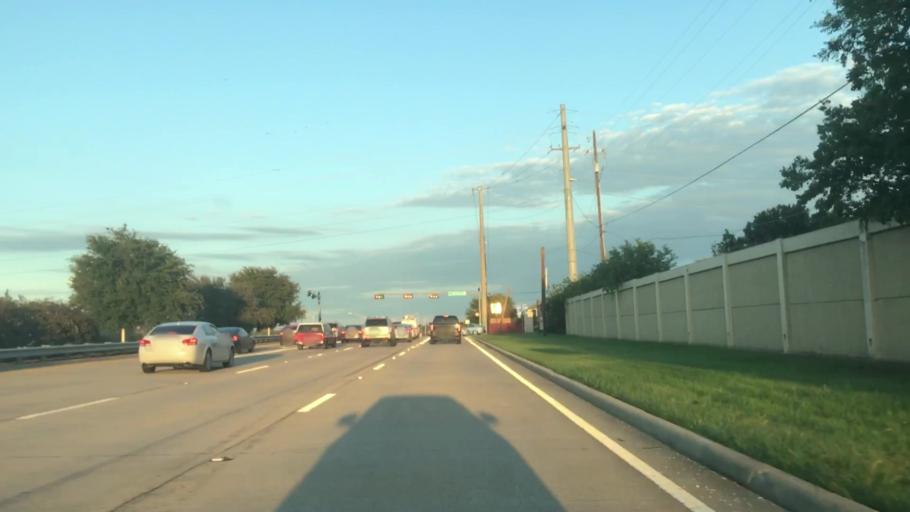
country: US
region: Texas
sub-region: Dallas County
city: Carrollton
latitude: 32.9838
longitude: -96.8983
